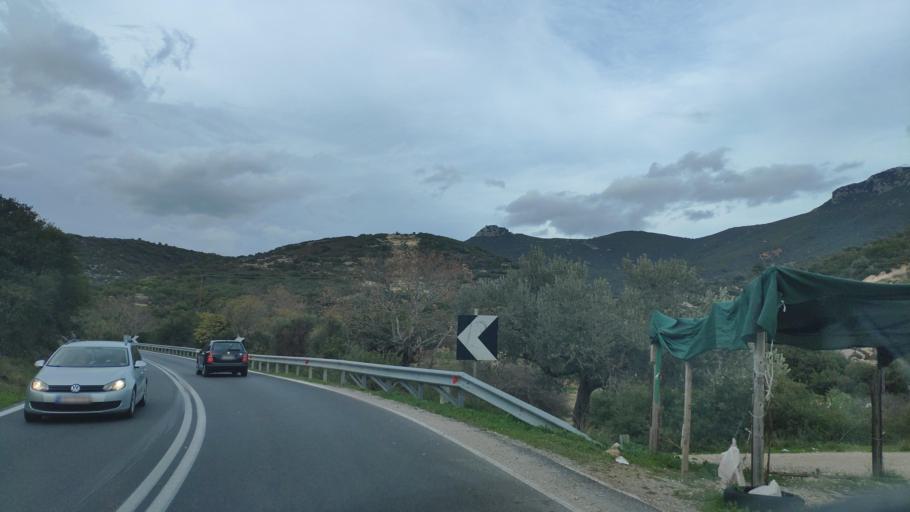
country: GR
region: Peloponnese
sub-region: Nomos Korinthias
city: Ayios Vasilios
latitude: 37.7620
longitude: 22.7314
